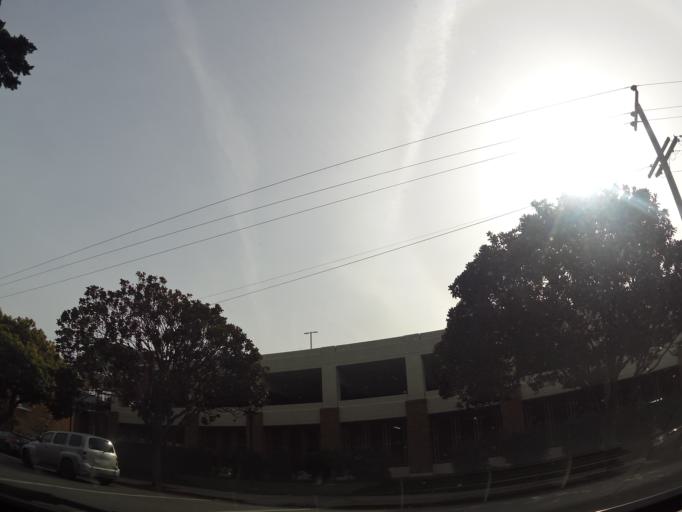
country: US
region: California
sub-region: Monterey County
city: Salinas
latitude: 36.6754
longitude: -121.6672
